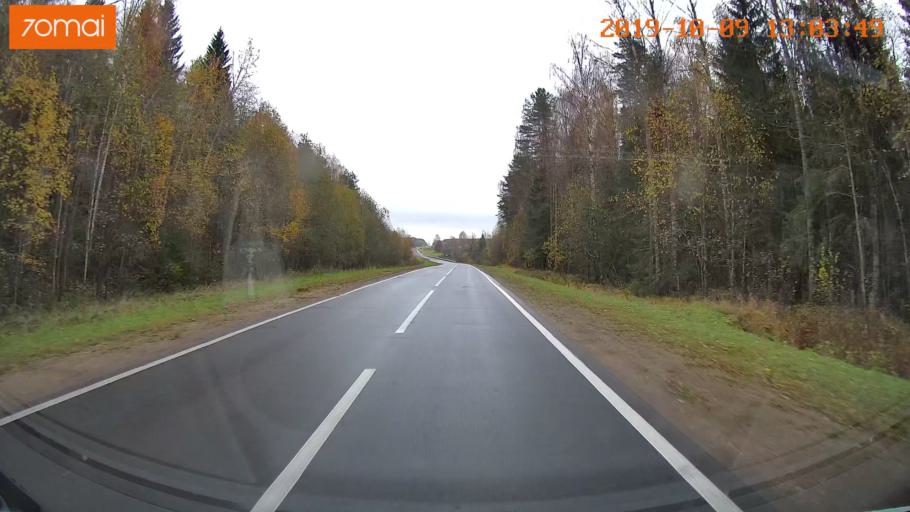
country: RU
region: Jaroslavl
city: Lyubim
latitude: 58.3591
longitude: 40.5377
